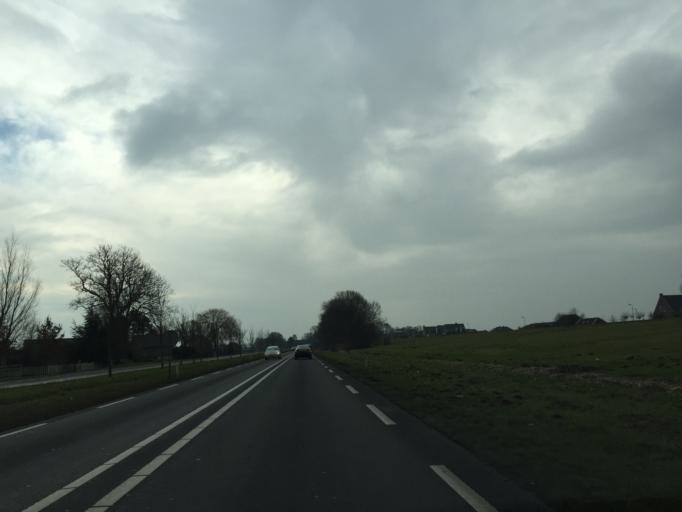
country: NL
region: South Holland
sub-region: Gemeente Lansingerland
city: Bleiswijk
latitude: 51.9954
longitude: 4.5947
